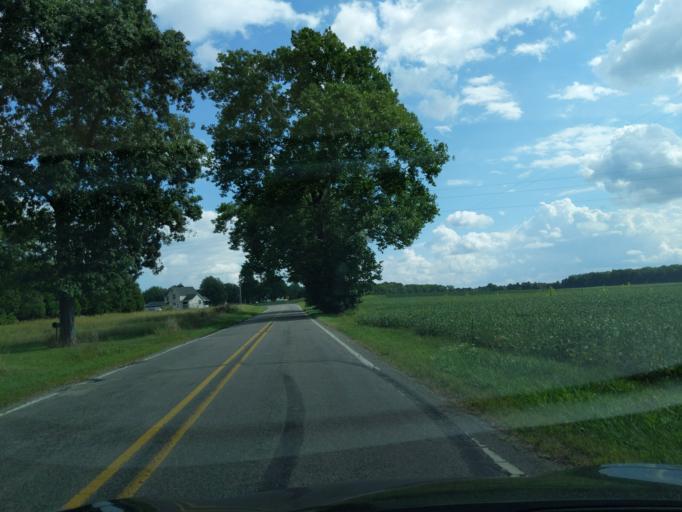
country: US
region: Michigan
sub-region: Jackson County
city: Spring Arbor
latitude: 42.3288
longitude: -84.5404
